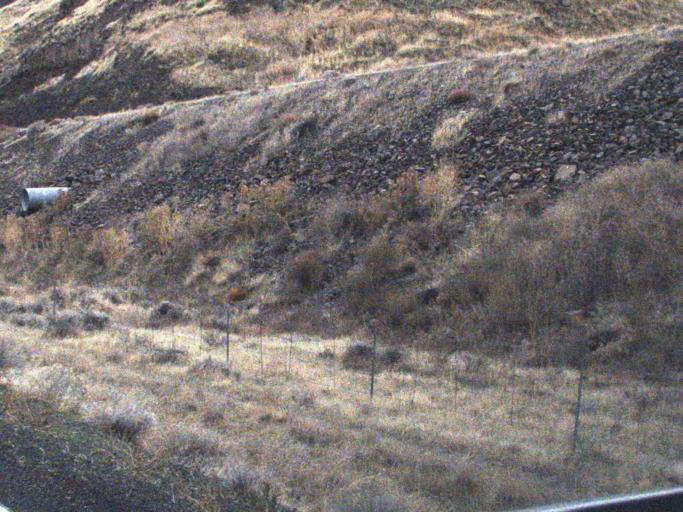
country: US
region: Washington
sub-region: Walla Walla County
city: Waitsburg
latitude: 46.5536
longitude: -118.1787
